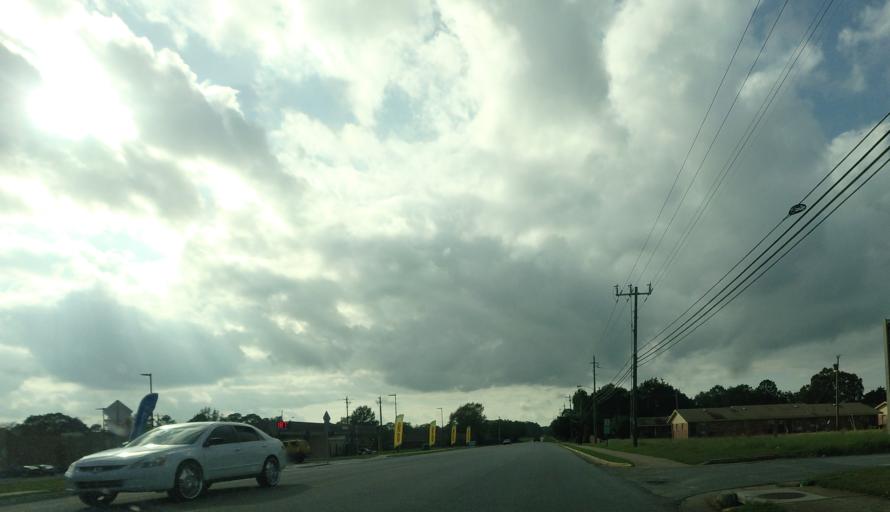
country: US
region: Georgia
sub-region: Houston County
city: Warner Robins
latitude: 32.6264
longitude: -83.6422
